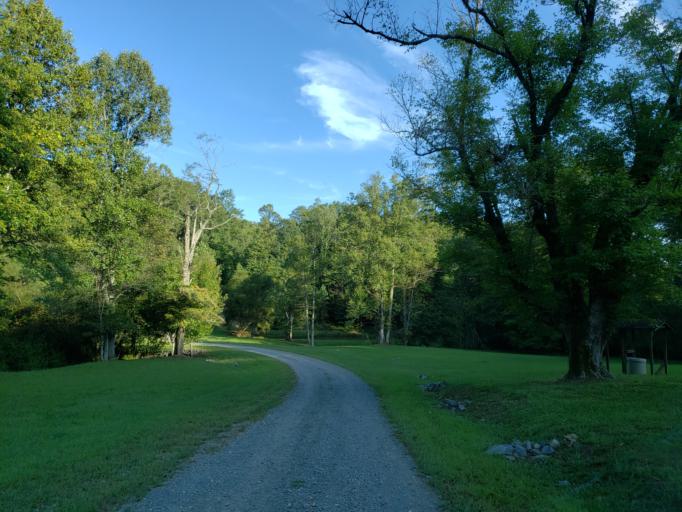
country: US
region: Georgia
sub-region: Fannin County
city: Blue Ridge
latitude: 34.6896
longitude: -84.2724
